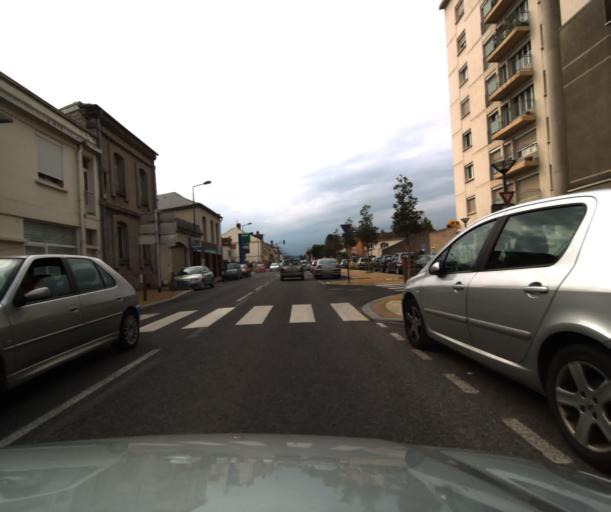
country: FR
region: Midi-Pyrenees
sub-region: Departement des Hautes-Pyrenees
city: Tarbes
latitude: 43.2329
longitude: 0.0923
